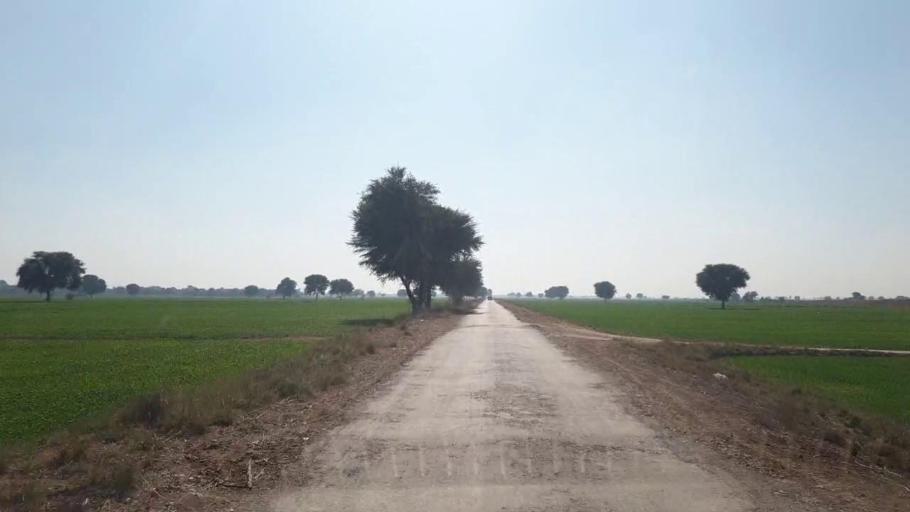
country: PK
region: Sindh
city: Shahpur Chakar
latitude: 26.1141
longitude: 68.6288
